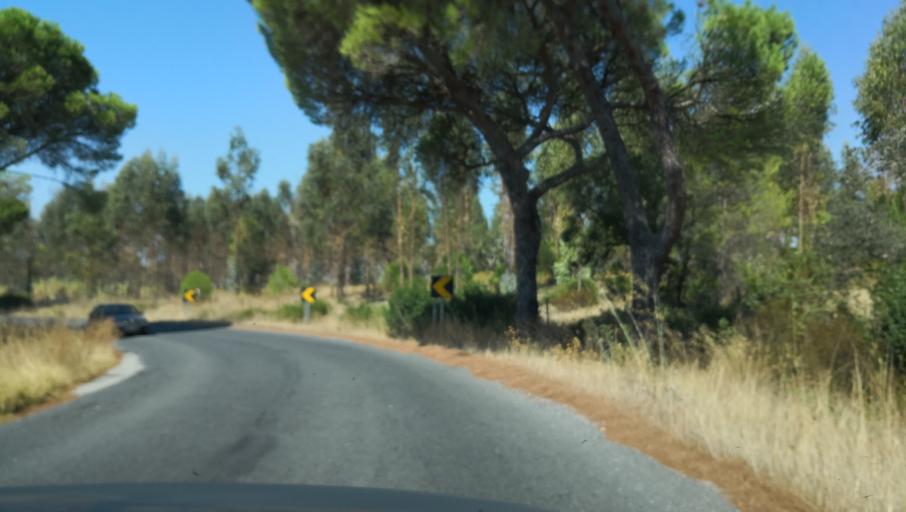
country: PT
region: Setubal
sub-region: Alcacer do Sal
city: Alcacer do Sal
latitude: 38.3039
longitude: -8.4075
